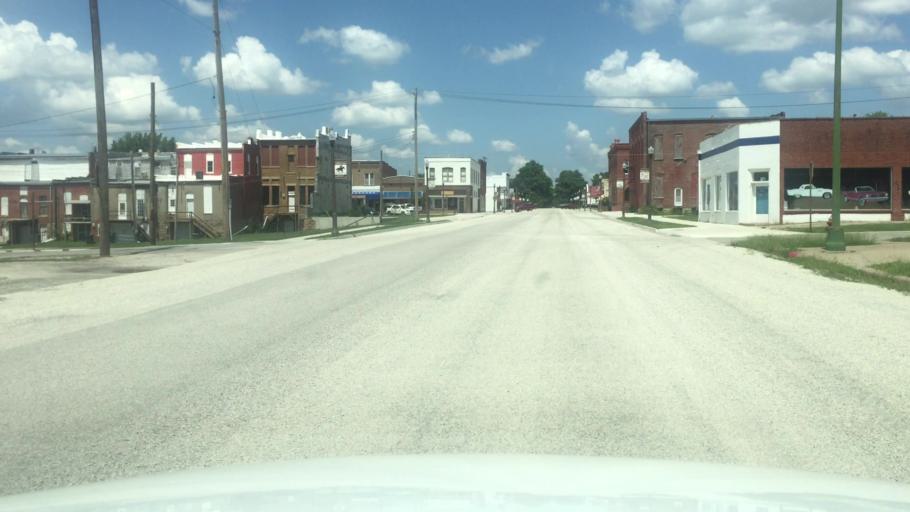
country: US
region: Kansas
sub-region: Brown County
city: Horton
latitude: 39.6588
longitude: -95.5274
